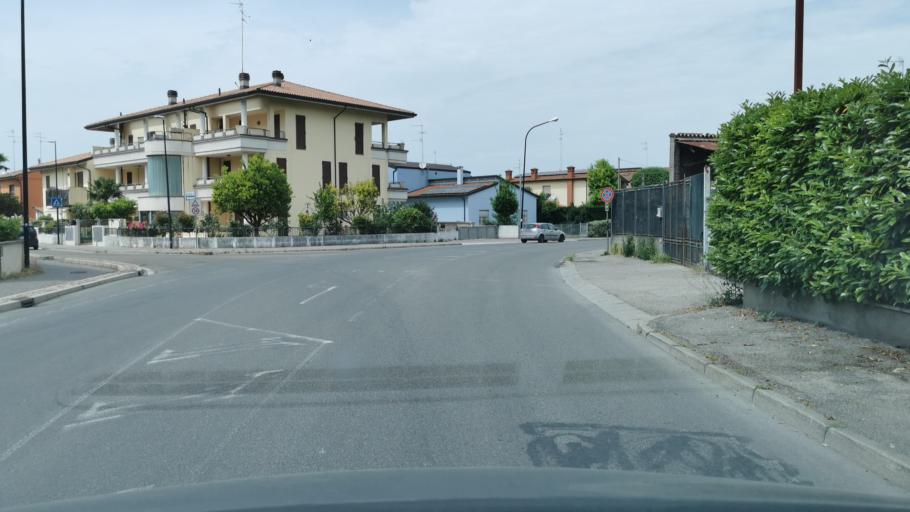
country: IT
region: Emilia-Romagna
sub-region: Provincia di Ravenna
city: Bagnacavallo
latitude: 44.4151
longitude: 11.9723
